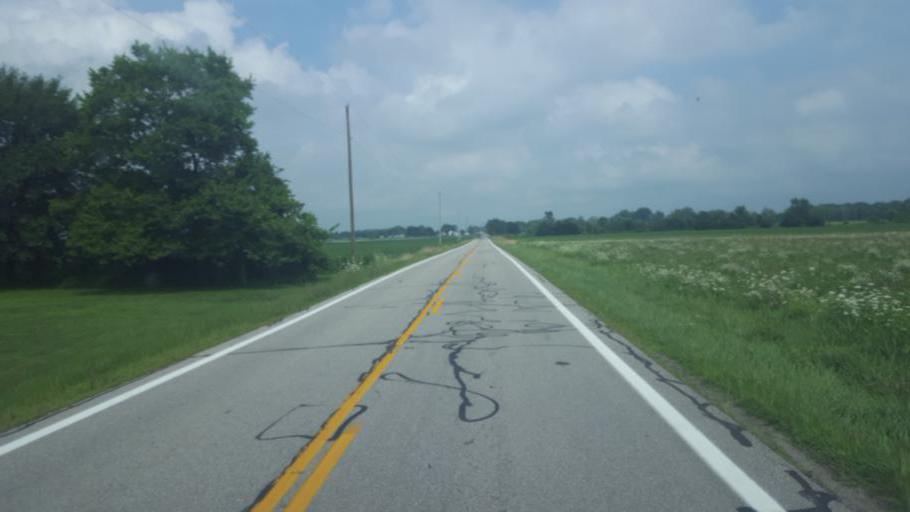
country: US
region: Ohio
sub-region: Union County
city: Richwood
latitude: 40.4811
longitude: -83.3289
